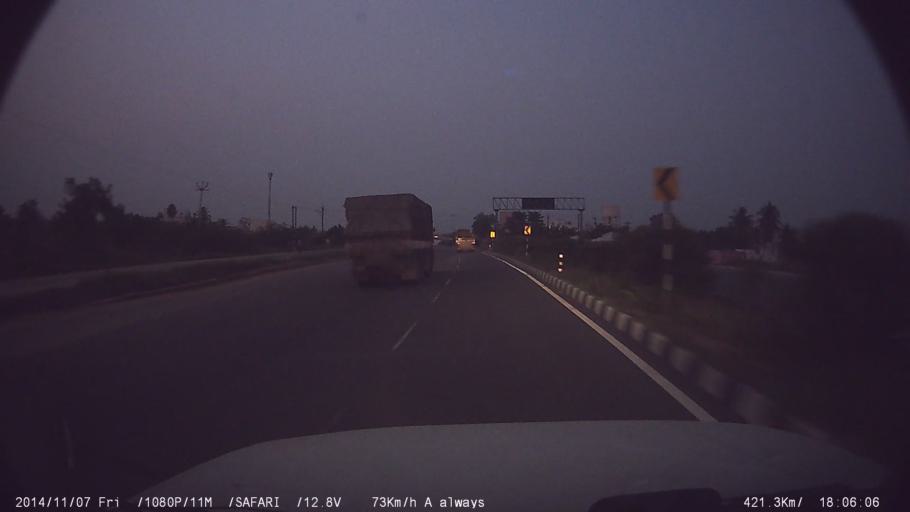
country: IN
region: Tamil Nadu
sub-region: Erode
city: Bhavani
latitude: 11.4174
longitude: 77.6764
